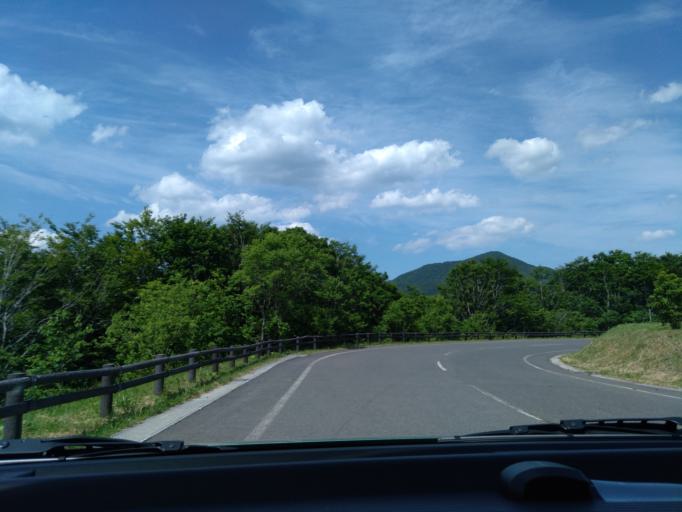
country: JP
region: Iwate
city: Ichinoseki
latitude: 39.0123
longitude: 140.8631
